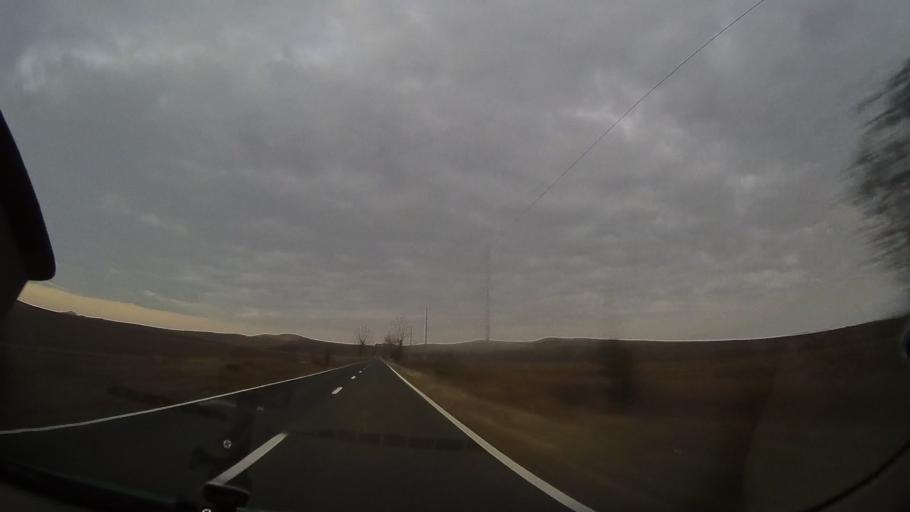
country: RO
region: Tulcea
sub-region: Comuna Nalbant
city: Nicolae Balcescu
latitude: 45.0065
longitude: 28.5978
